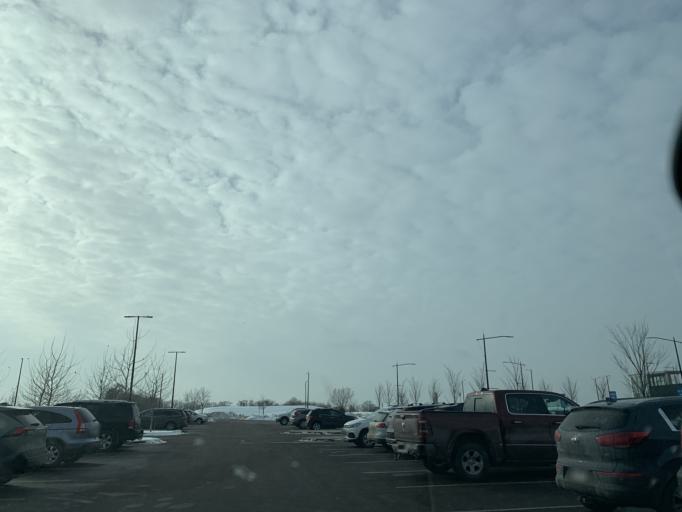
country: US
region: Minnesota
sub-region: Dakota County
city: Mendota Heights
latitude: 44.8580
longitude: -93.1163
